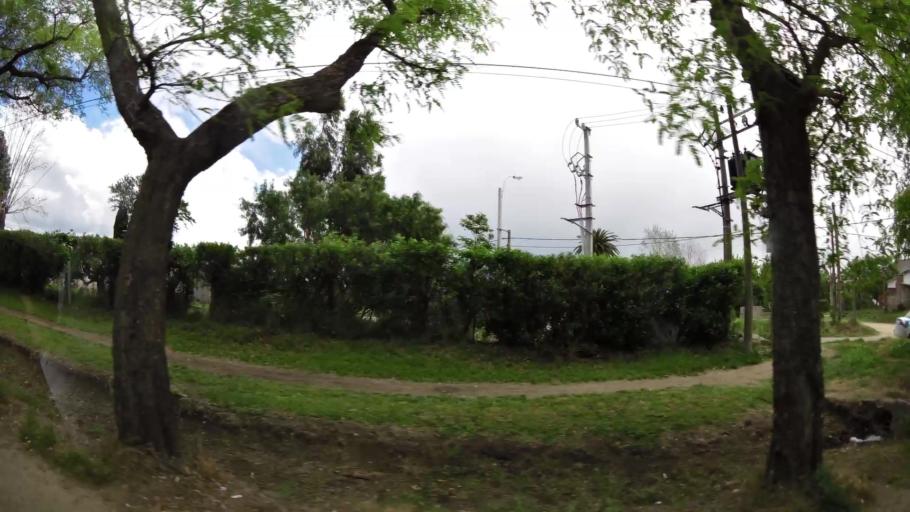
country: UY
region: Canelones
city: La Paz
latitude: -34.8030
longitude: -56.1587
